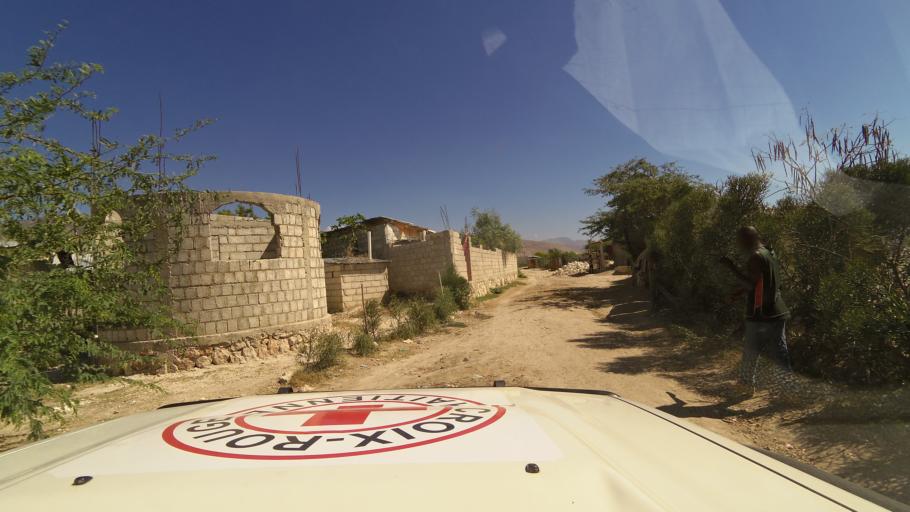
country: HT
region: Ouest
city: Croix des Bouquets
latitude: 18.6524
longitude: -72.2554
